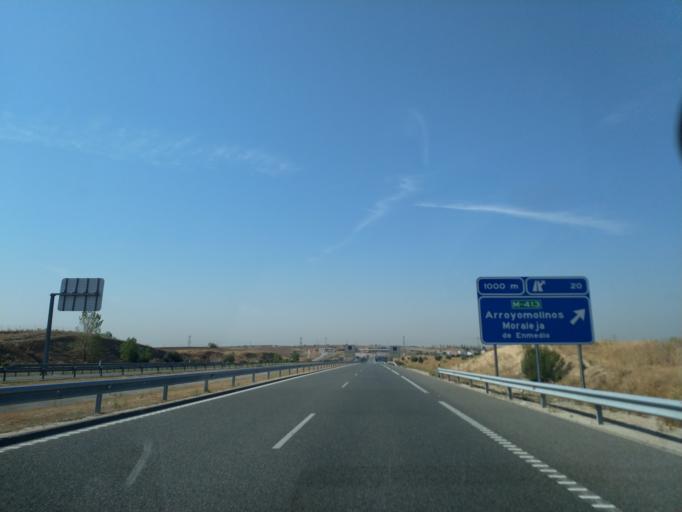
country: ES
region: Madrid
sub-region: Provincia de Madrid
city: Arroyomolinos
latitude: 40.2662
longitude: -3.8993
